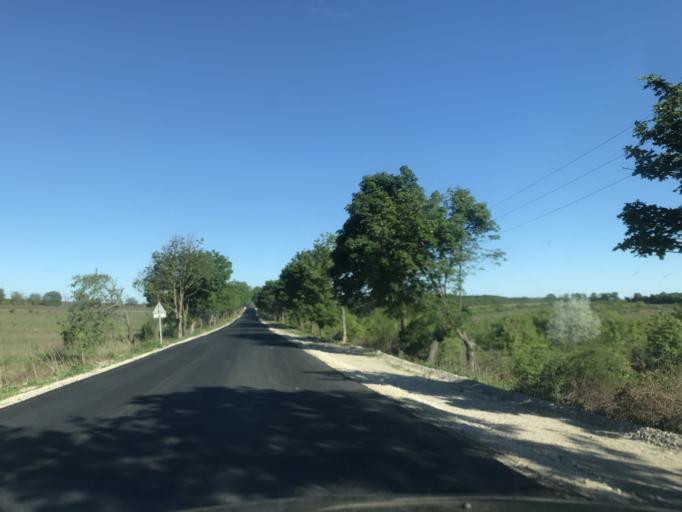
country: MD
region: Chisinau
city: Cricova
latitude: 47.2542
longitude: 28.8069
